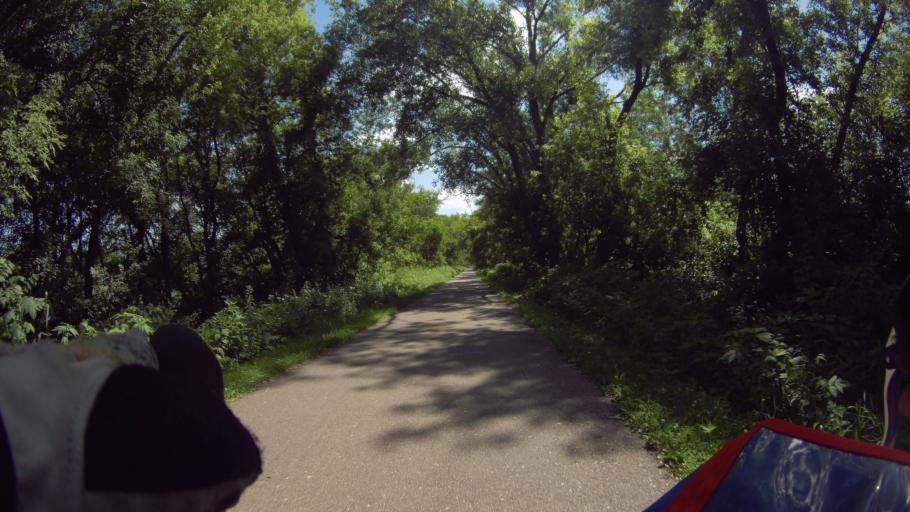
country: US
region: Wisconsin
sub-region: Dane County
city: Fitchburg
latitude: 42.9462
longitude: -89.4790
